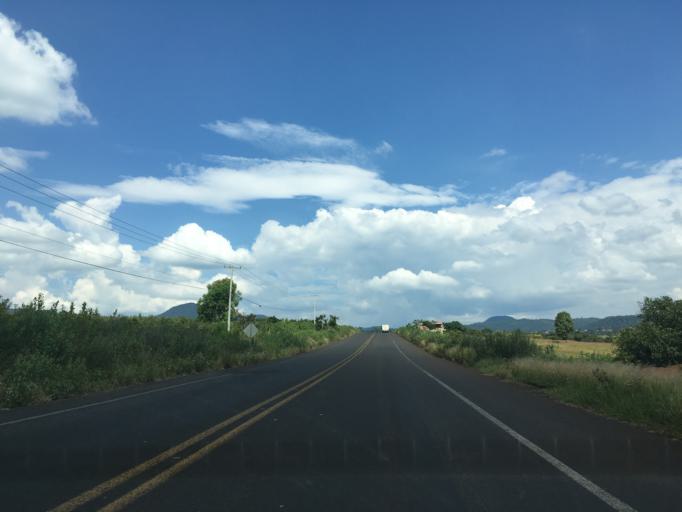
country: MX
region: Michoacan
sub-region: Tingueindin
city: Tingueindin
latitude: 19.8386
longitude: -102.4906
